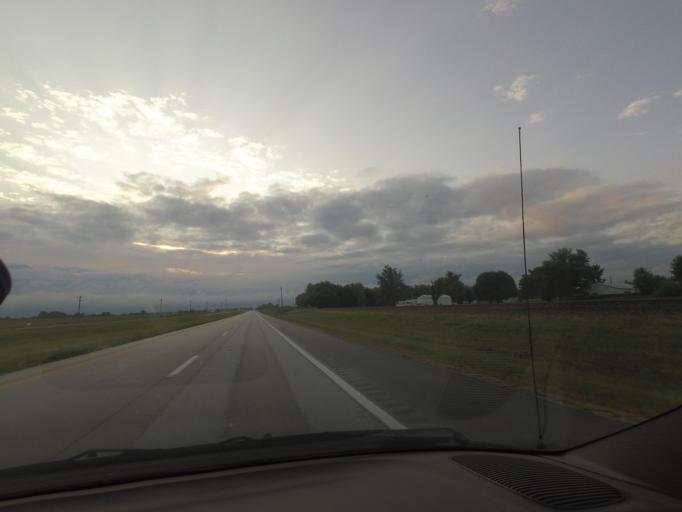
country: US
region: Missouri
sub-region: Shelby County
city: Shelbina
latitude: 39.7024
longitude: -92.0772
